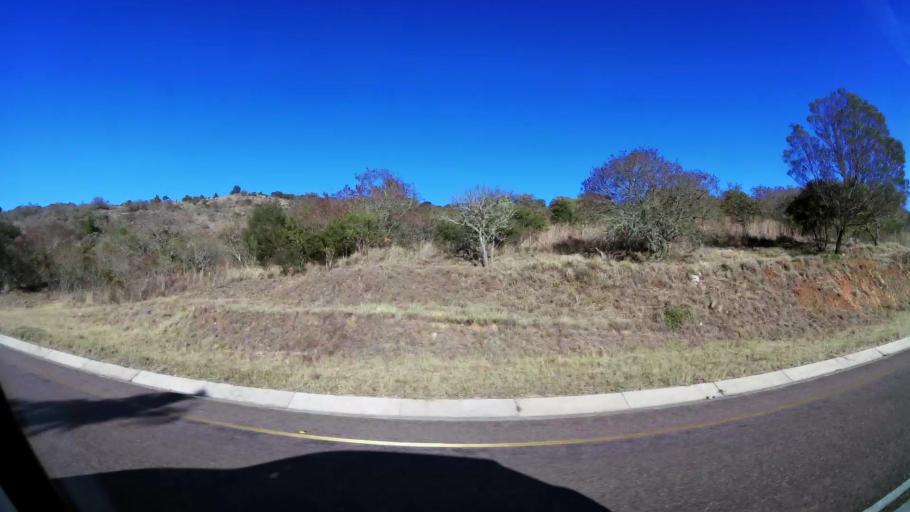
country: ZA
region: Limpopo
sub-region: Capricorn District Municipality
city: Mankoeng
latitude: -23.9264
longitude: 29.8940
